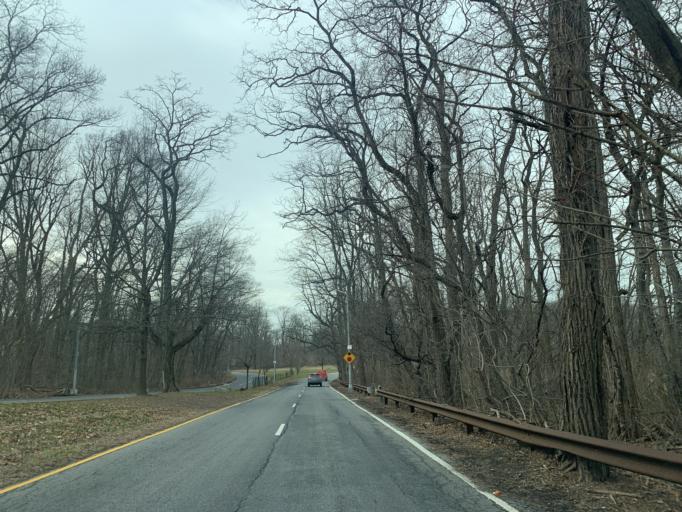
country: US
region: New York
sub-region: Westchester County
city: Pelham Manor
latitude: 40.8679
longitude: -73.8085
